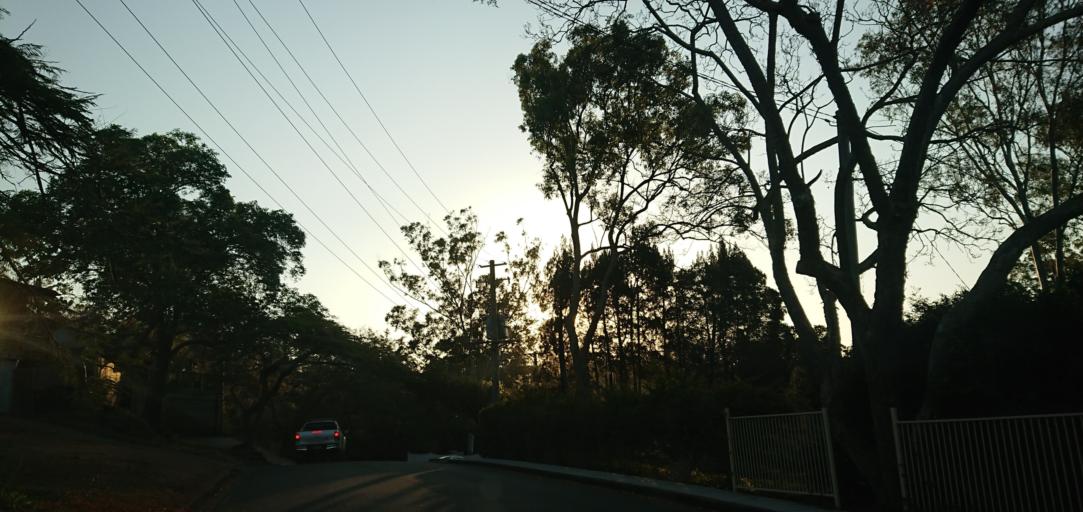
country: AU
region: Queensland
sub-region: Brisbane
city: Taringa
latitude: -27.5042
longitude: 152.9586
